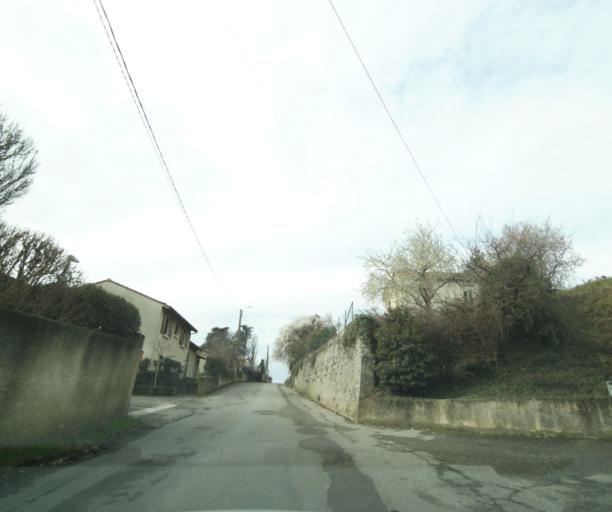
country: FR
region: Rhone-Alpes
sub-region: Departement de la Drome
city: Bourg-les-Valence
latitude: 44.9471
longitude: 4.9095
